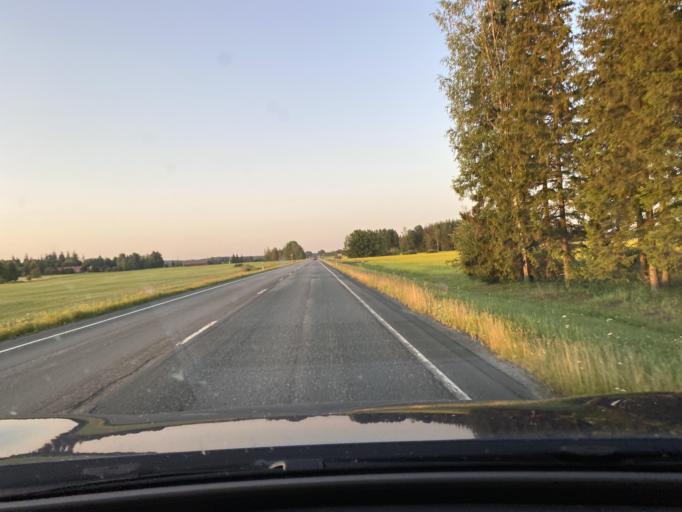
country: FI
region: Haeme
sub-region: Forssa
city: Humppila
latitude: 60.9472
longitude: 23.3129
